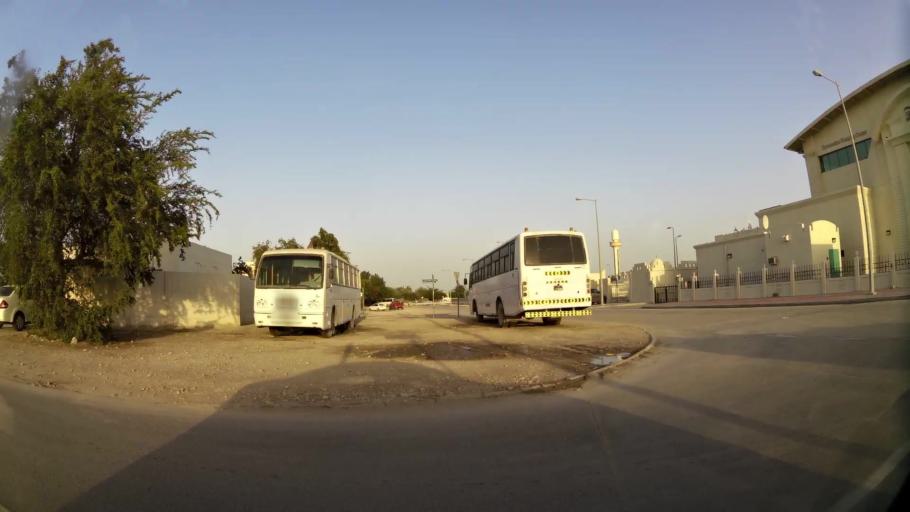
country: QA
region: Baladiyat ar Rayyan
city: Ar Rayyan
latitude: 25.3163
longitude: 51.4582
